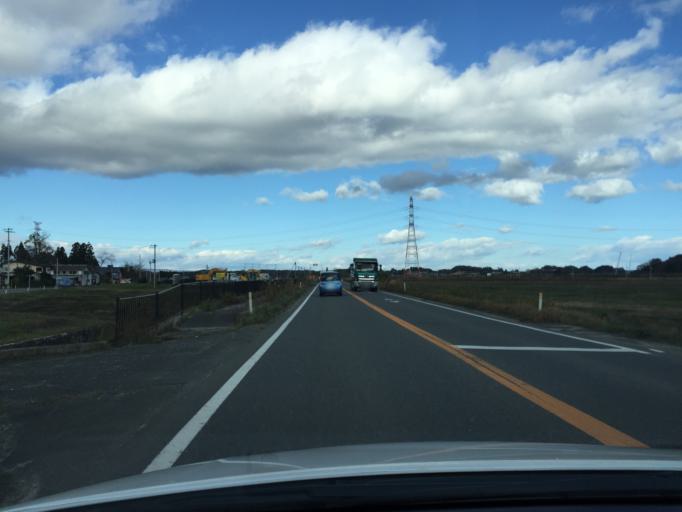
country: JP
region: Fukushima
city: Namie
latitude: 37.5909
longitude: 141.0048
